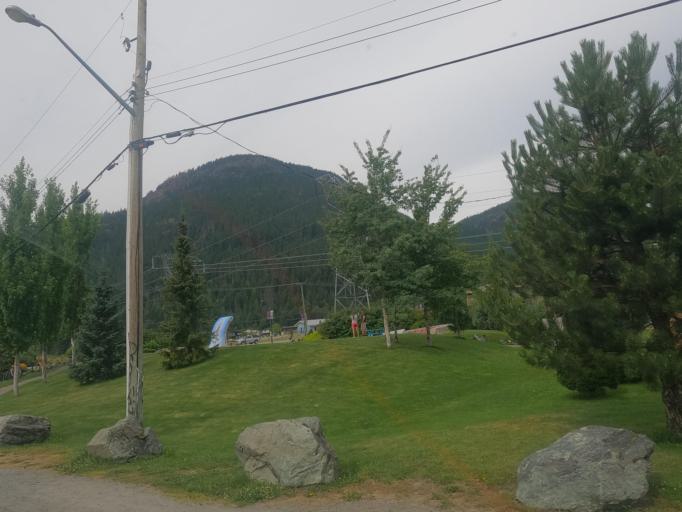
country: CA
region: British Columbia
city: Pemberton
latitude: 50.3192
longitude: -122.8009
